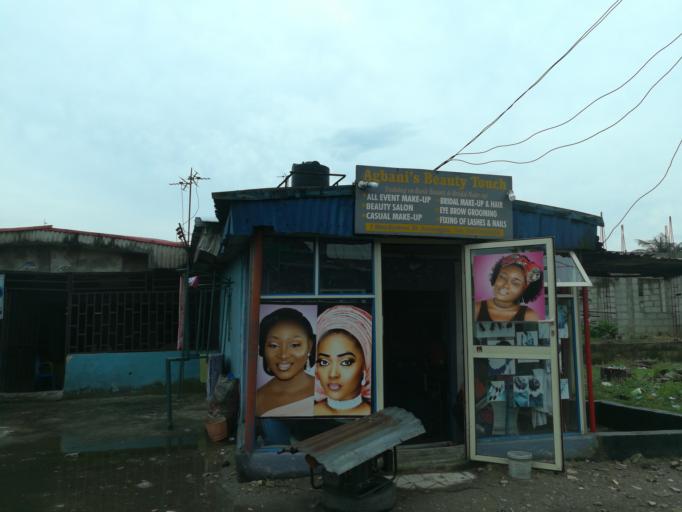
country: NG
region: Rivers
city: Port Harcourt
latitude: 4.8460
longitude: 7.0367
